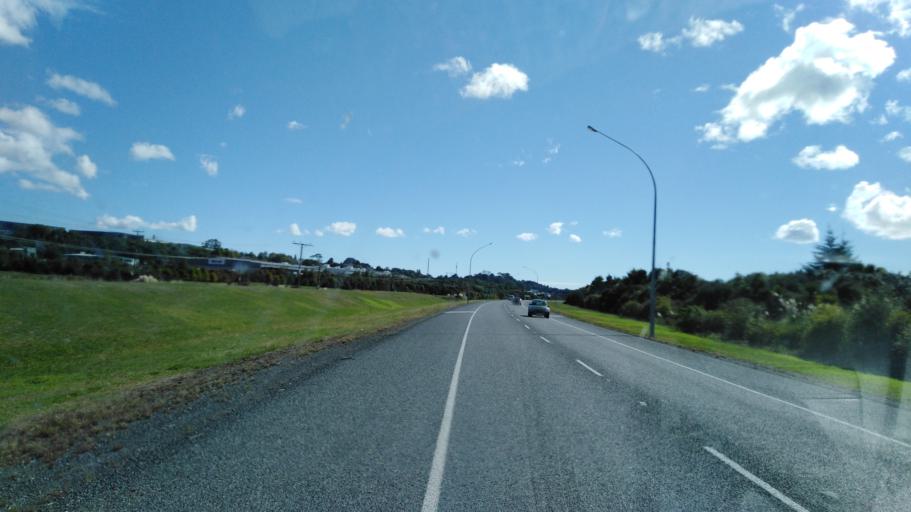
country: NZ
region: Bay of Plenty
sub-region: Tauranga City
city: Tauranga
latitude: -37.7467
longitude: 176.1038
